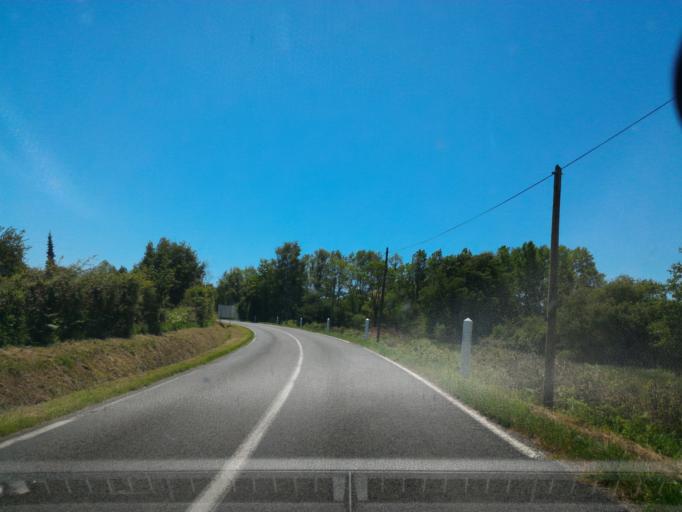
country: FR
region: Poitou-Charentes
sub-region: Departement de la Vienne
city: Availles-Limouzine
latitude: 46.1860
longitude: 0.7254
